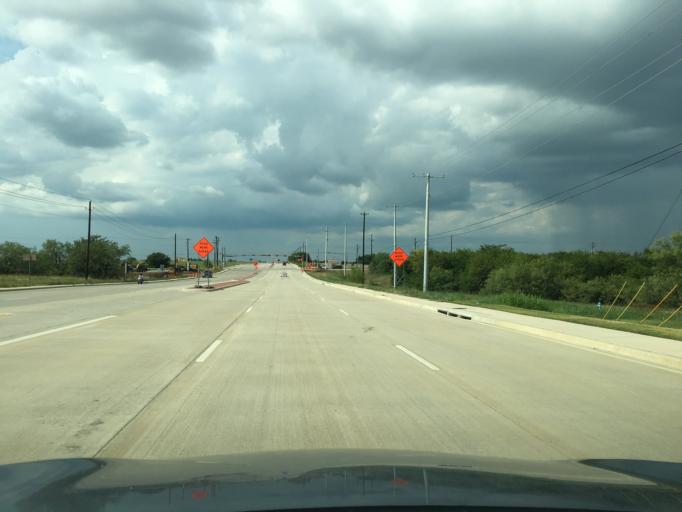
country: US
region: Texas
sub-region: Denton County
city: Oak Point
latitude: 33.1842
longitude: -96.9769
